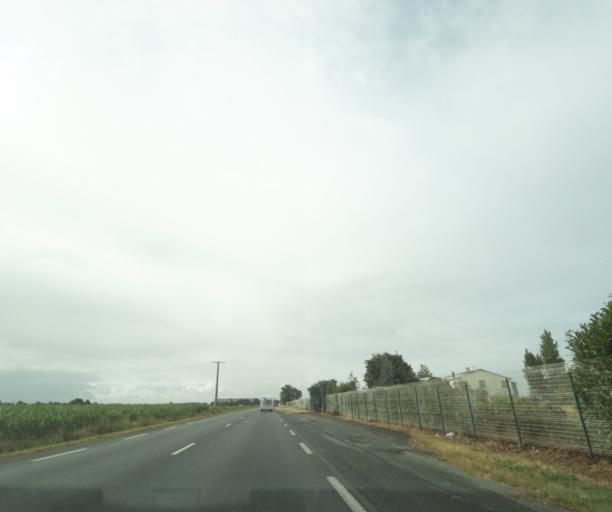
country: FR
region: Pays de la Loire
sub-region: Departement de la Vendee
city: Sainte-Gemme-la-Plaine
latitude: 46.4588
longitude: -1.1062
